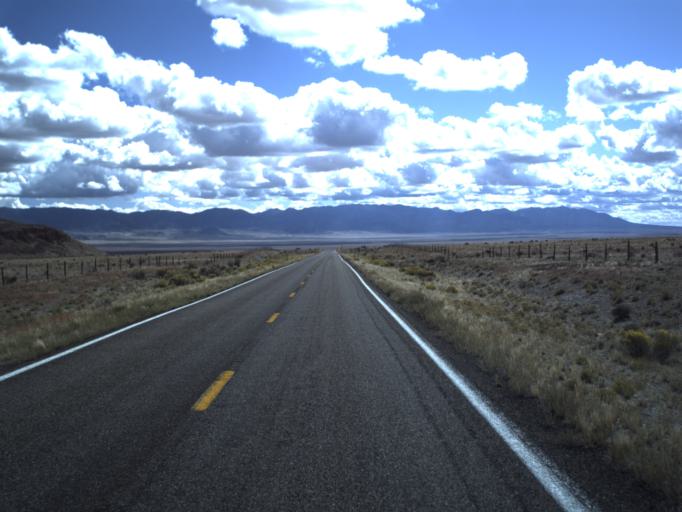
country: US
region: Utah
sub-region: Beaver County
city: Milford
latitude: 38.5920
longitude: -113.8213
